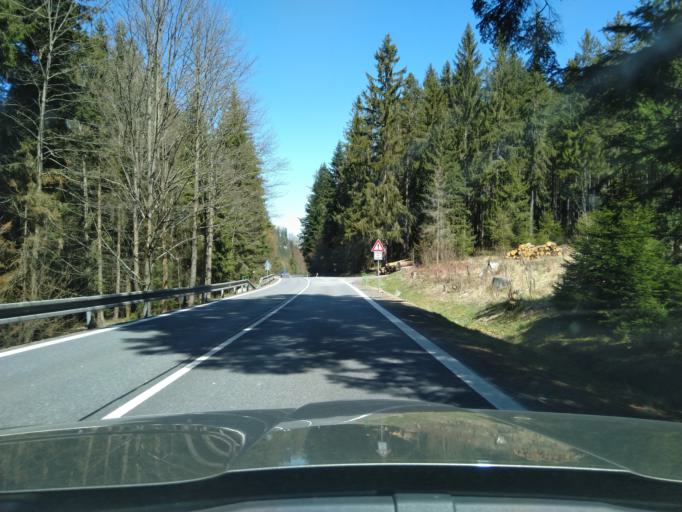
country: CZ
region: Jihocesky
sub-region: Okres Prachatice
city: Vimperk
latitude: 49.0409
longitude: 13.7606
